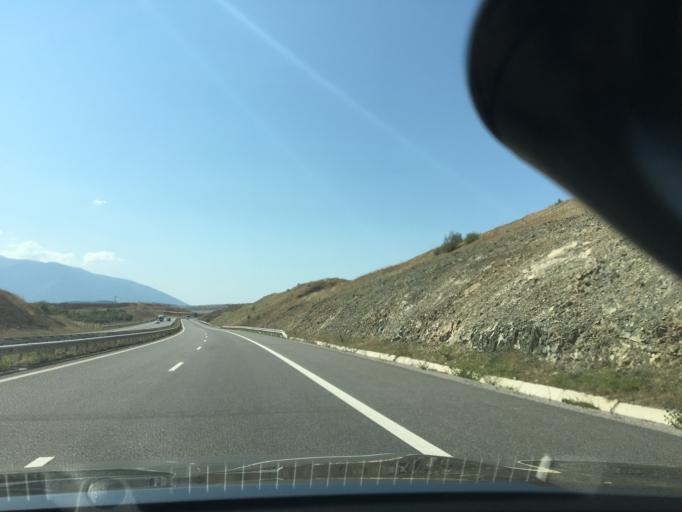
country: BG
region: Kyustendil
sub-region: Obshtina Dupnitsa
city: Dupnitsa
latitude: 42.3197
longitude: 23.0951
